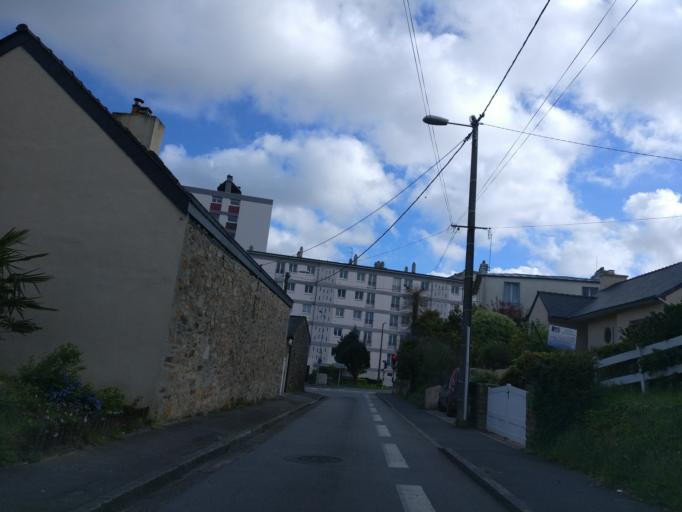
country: FR
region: Brittany
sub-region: Departement du Finistere
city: Brest
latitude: 48.4021
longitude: -4.4567
